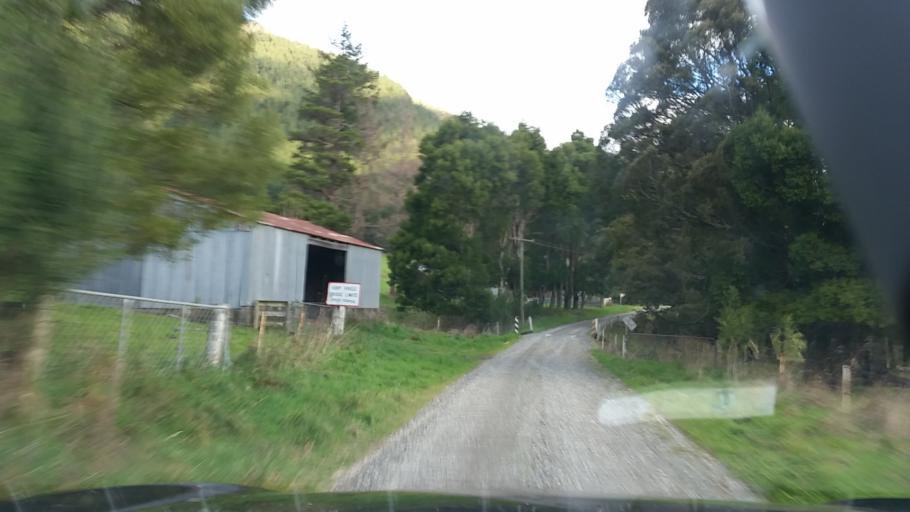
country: NZ
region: Nelson
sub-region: Nelson City
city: Nelson
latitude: -41.1789
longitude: 173.6493
